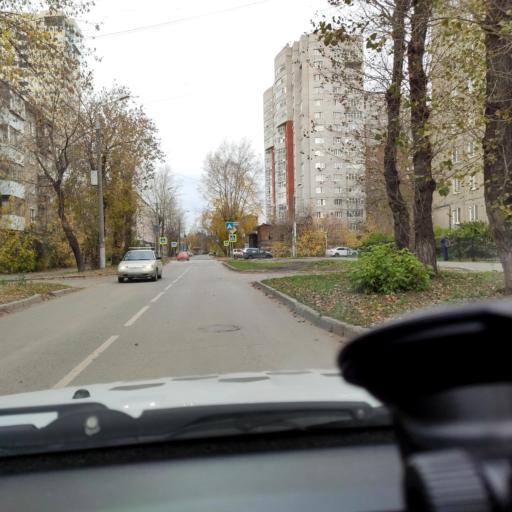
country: RU
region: Perm
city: Perm
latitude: 58.0094
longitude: 56.2036
